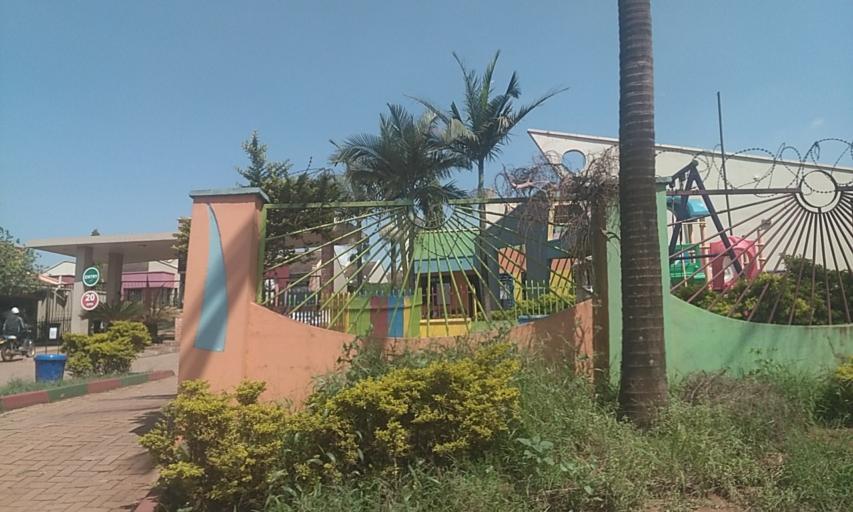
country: UG
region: Central Region
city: Kampala Central Division
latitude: 0.3906
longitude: 32.5928
